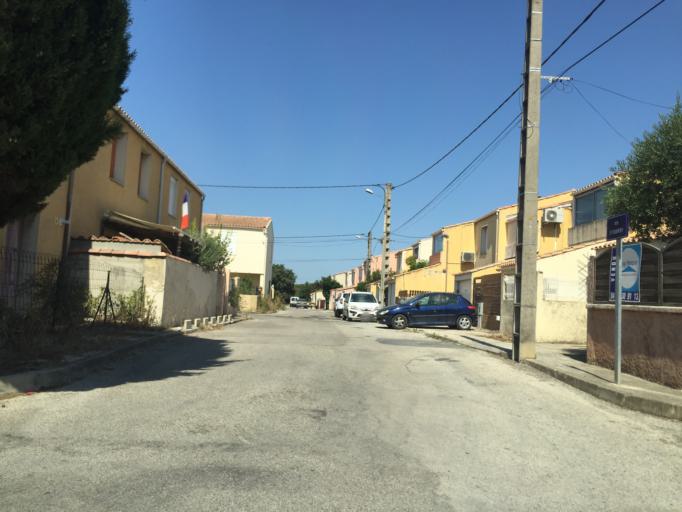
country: FR
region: Provence-Alpes-Cote d'Azur
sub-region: Departement du Vaucluse
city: Orange
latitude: 44.1189
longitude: 4.8291
